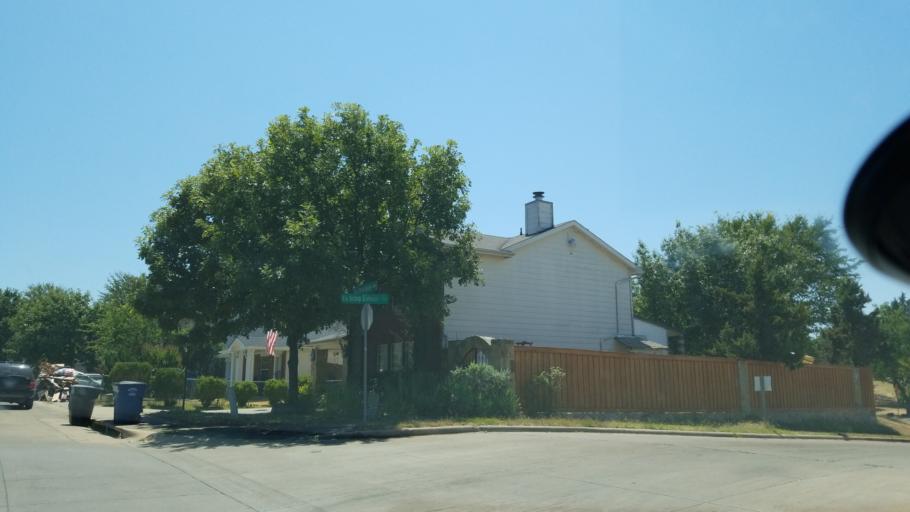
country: US
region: Texas
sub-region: Dallas County
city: Cockrell Hill
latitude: 32.7376
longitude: -96.8958
